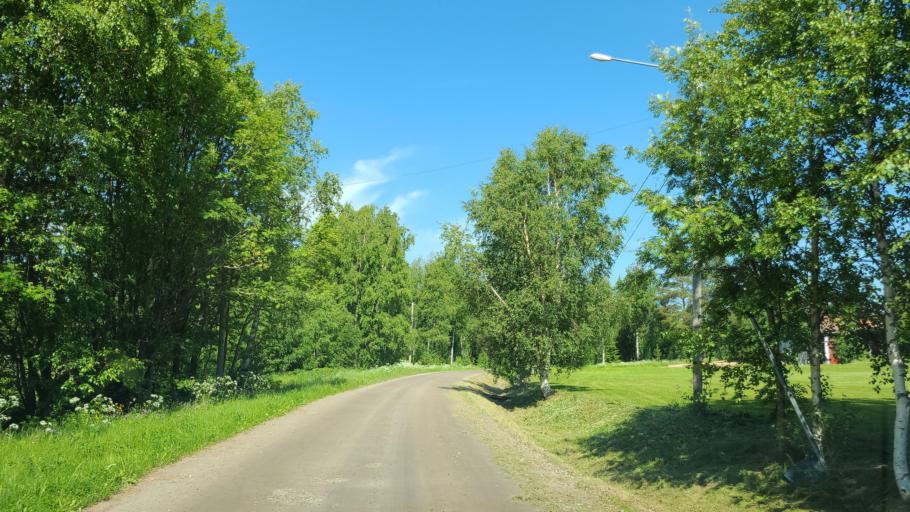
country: SE
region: Vaesterbotten
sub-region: Robertsfors Kommun
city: Robertsfors
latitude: 64.0849
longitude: 20.8431
